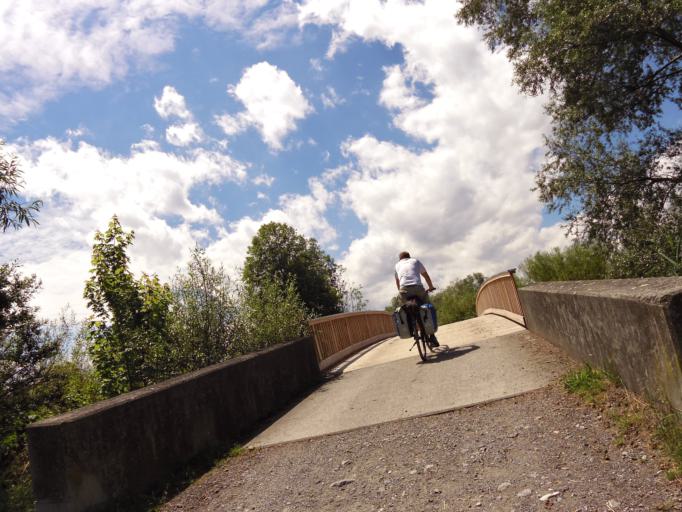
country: AT
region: Vorarlberg
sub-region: Politischer Bezirk Bregenz
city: Hard
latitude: 47.4935
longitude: 9.6762
